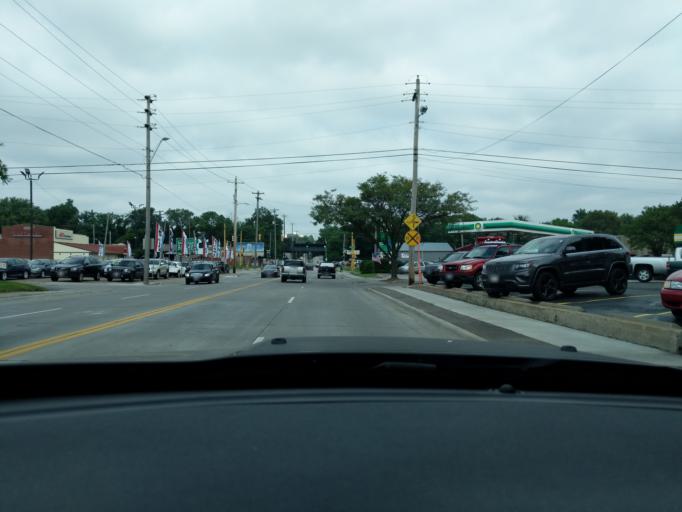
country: US
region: Iowa
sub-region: Scott County
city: Davenport
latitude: 41.5226
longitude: -90.6012
